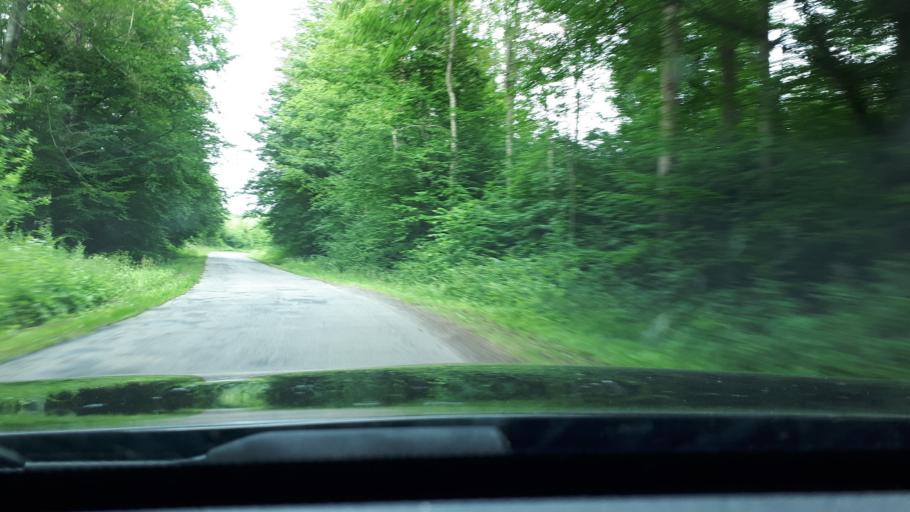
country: PL
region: Warmian-Masurian Voivodeship
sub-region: Powiat ostrodzki
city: Gierzwald
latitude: 53.6393
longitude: 20.0892
